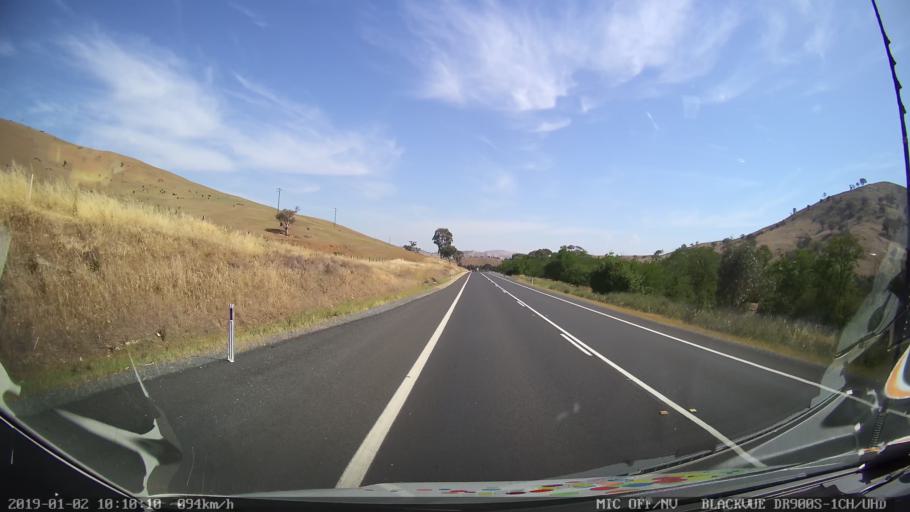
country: AU
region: New South Wales
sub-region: Gundagai
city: Gundagai
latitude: -35.1075
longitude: 148.0969
